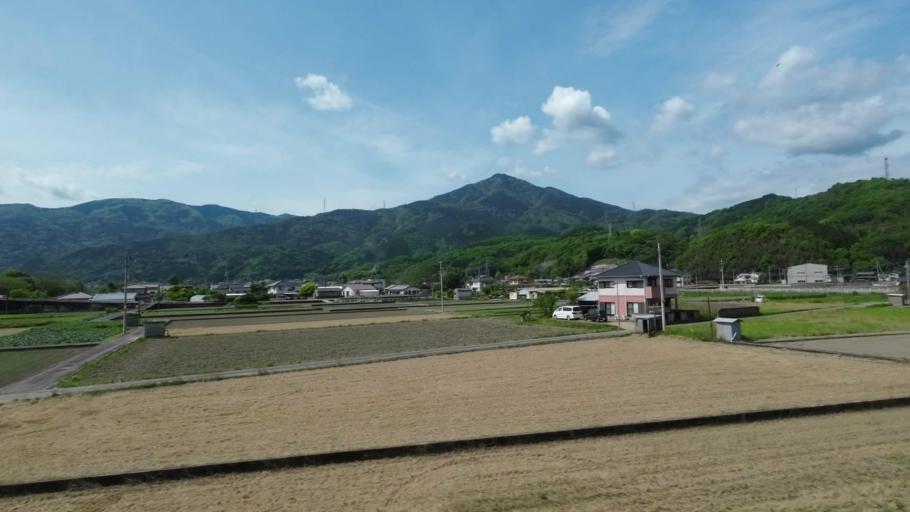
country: JP
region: Tokushima
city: Wakimachi
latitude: 34.0559
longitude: 134.2247
